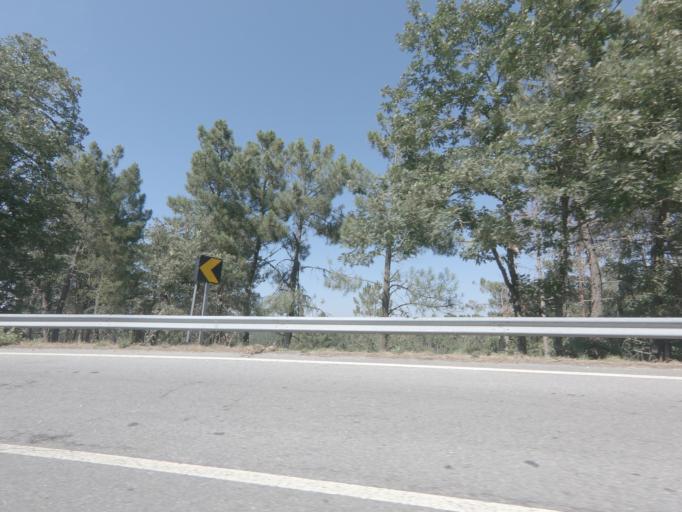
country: PT
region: Viseu
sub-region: Moimenta da Beira
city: Moimenta da Beira
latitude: 41.0045
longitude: -7.6958
